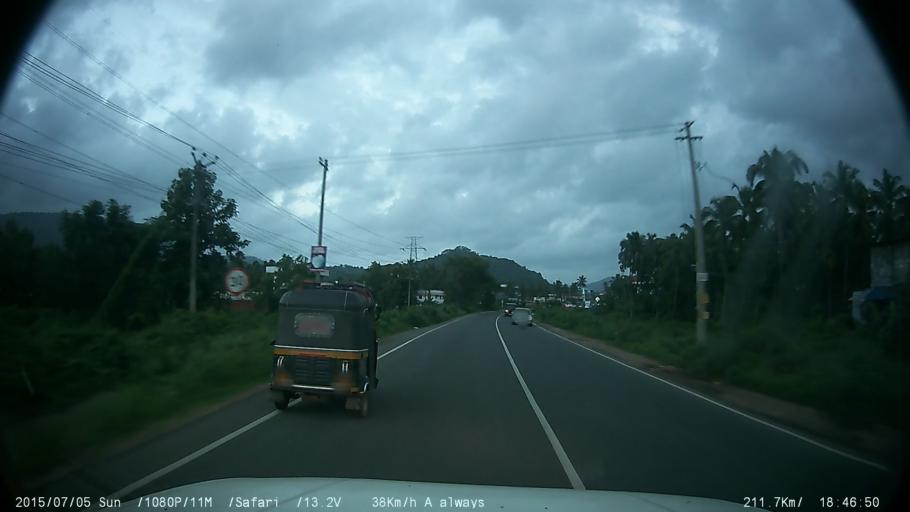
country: IN
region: Kerala
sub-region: Thrissur District
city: Trichur
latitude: 10.5560
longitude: 76.3198
